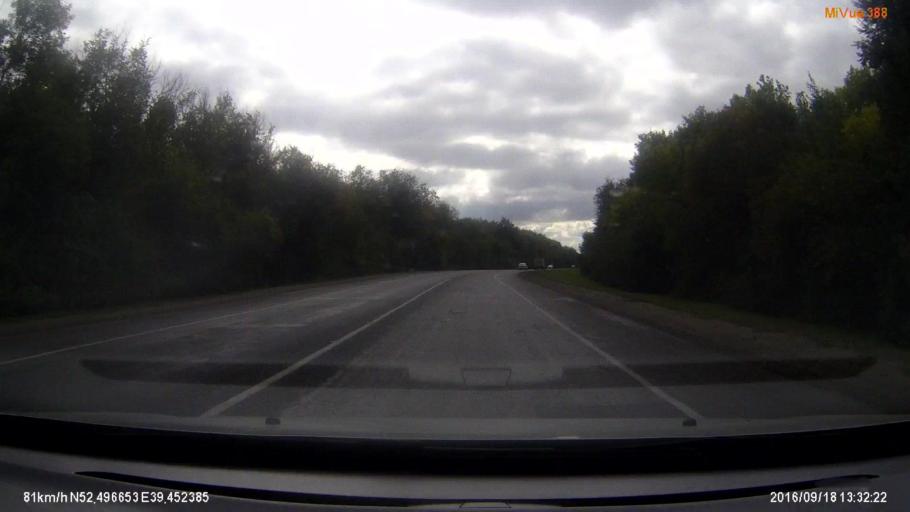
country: RU
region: Lipetsk
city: Borinskoye
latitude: 52.4686
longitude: 39.4176
